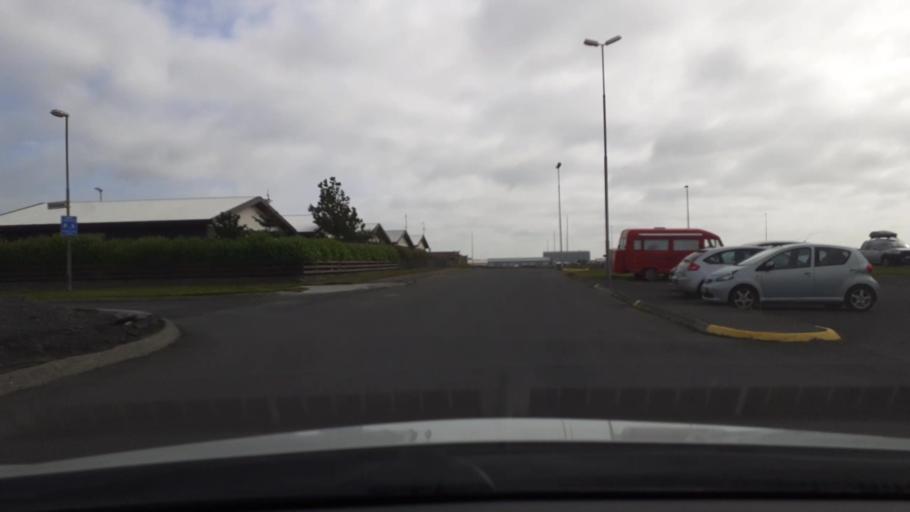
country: IS
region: South
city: THorlakshoefn
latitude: 63.8574
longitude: -21.3913
